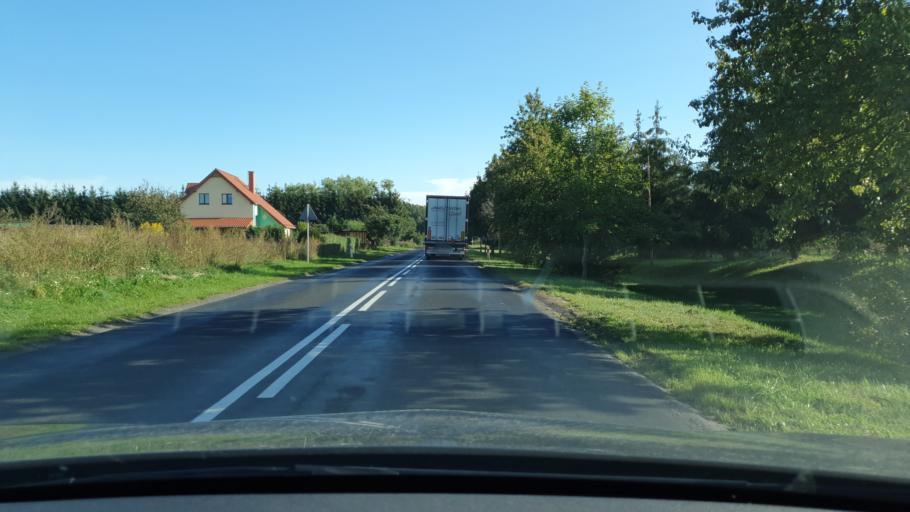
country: PL
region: West Pomeranian Voivodeship
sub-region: Powiat kamienski
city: Golczewo
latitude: 53.8206
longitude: 14.9891
